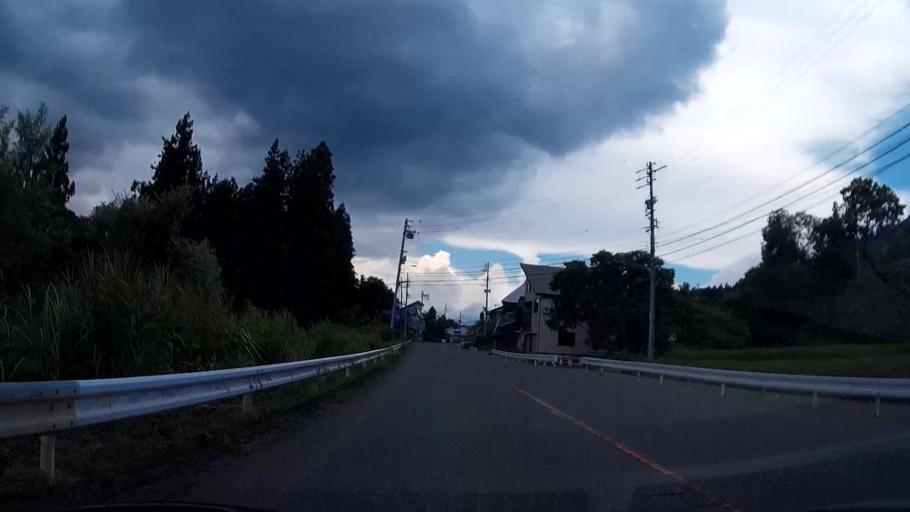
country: JP
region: Nagano
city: Iiyama
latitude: 36.9854
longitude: 138.5374
